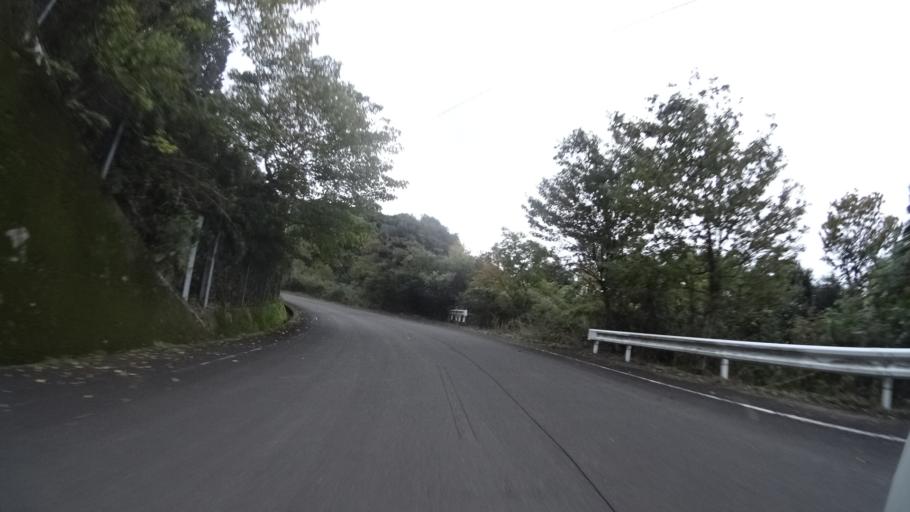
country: JP
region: Kyoto
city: Maizuru
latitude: 35.5665
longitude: 135.4631
